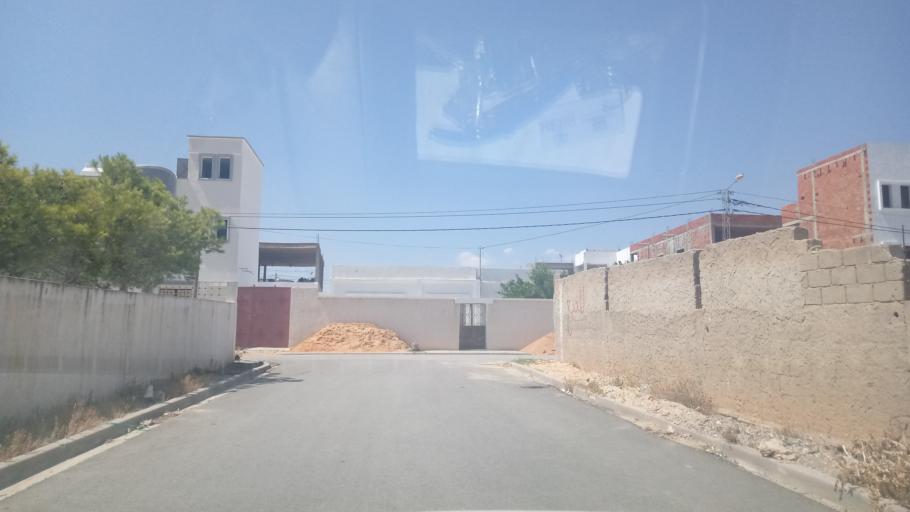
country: TN
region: Al Qayrawan
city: Sbikha
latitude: 36.1173
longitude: 10.0908
